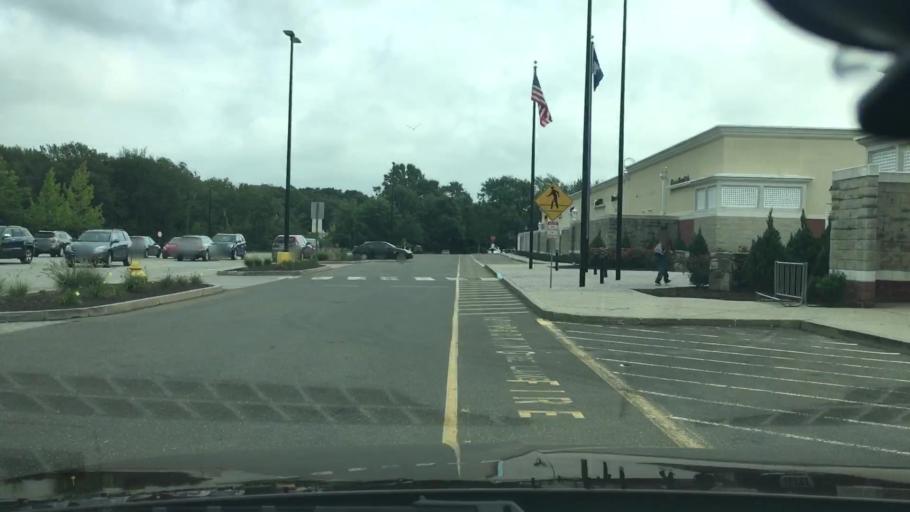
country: US
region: Connecticut
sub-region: Middlesex County
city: Clinton
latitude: 41.2920
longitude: -72.5335
